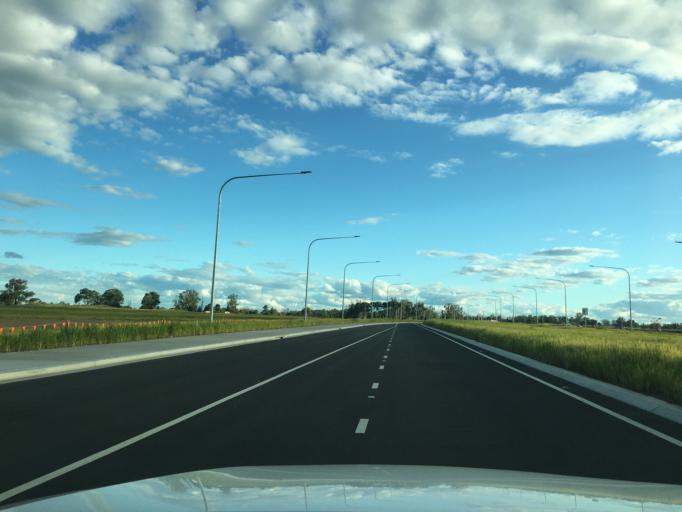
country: AU
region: New South Wales
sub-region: Liverpool
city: Bringelly
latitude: -33.8794
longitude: 150.7463
